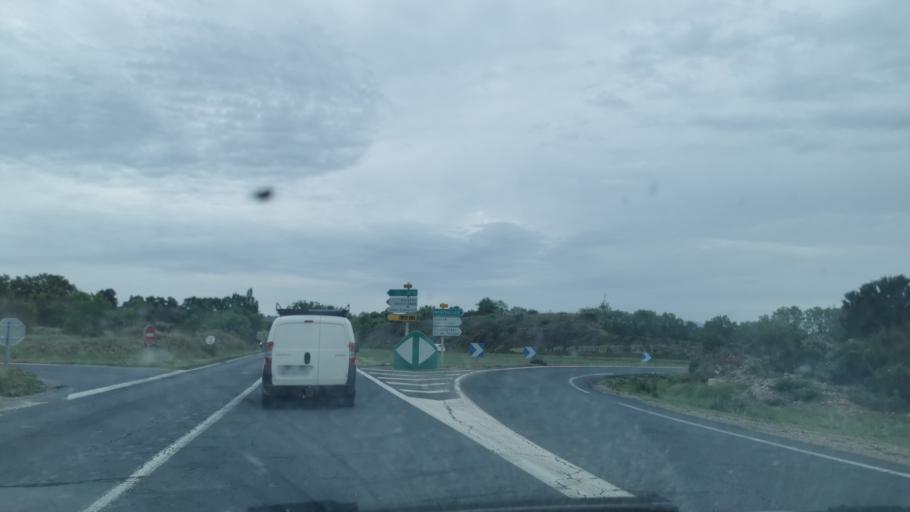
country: FR
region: Languedoc-Roussillon
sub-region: Departement de l'Herault
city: Balaruc-le-Vieux
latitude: 43.4729
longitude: 3.6871
